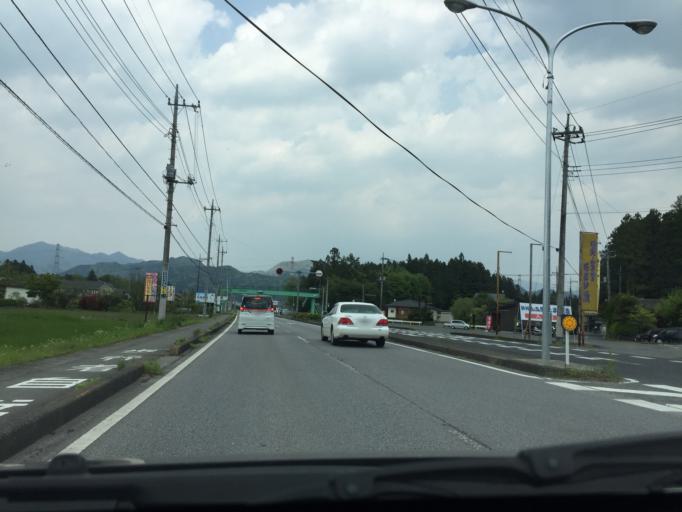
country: JP
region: Tochigi
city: Imaichi
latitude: 36.7567
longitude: 139.7161
